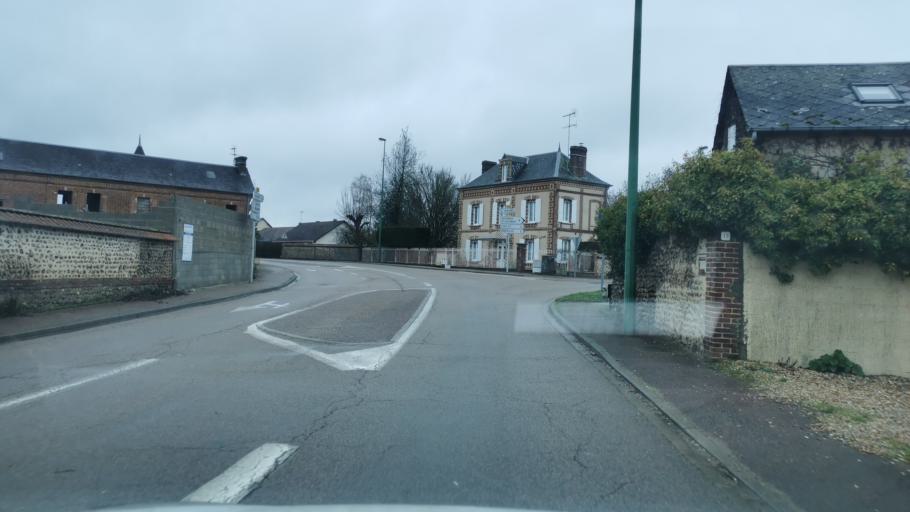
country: FR
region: Haute-Normandie
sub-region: Departement de l'Eure
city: Normanville
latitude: 49.0823
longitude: 1.1815
